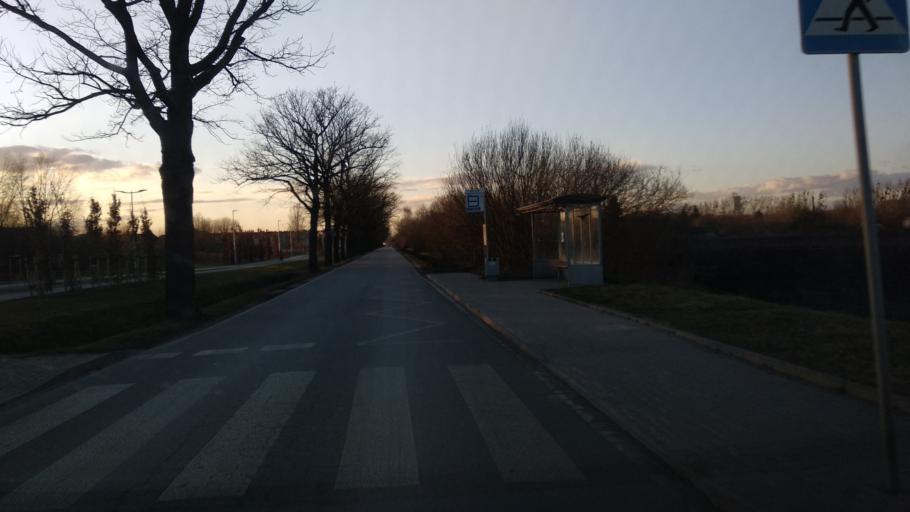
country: PL
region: Lower Silesian Voivodeship
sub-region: Powiat wroclawski
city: Zerniki Wroclawskie
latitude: 51.0650
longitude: 17.0652
